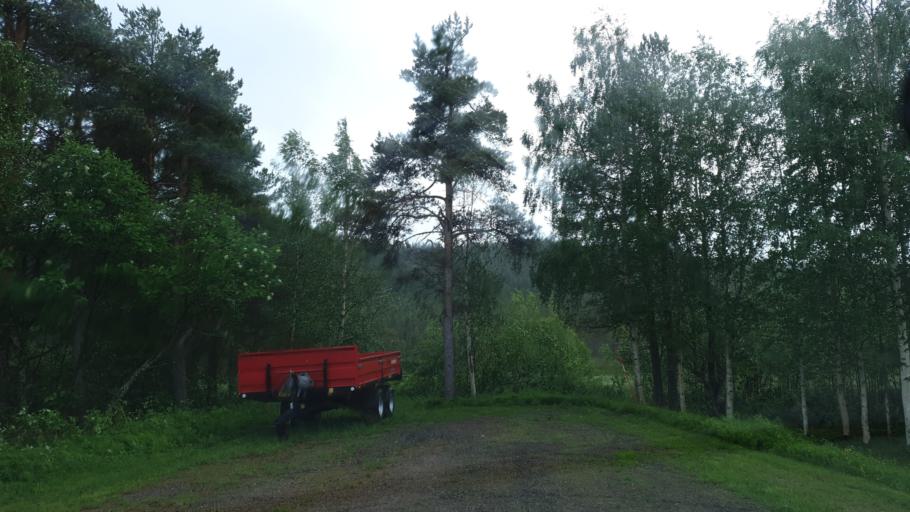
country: SE
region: Norrbotten
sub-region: Arvidsjaurs Kommun
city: Arvidsjaur
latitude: 65.7041
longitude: 18.7165
